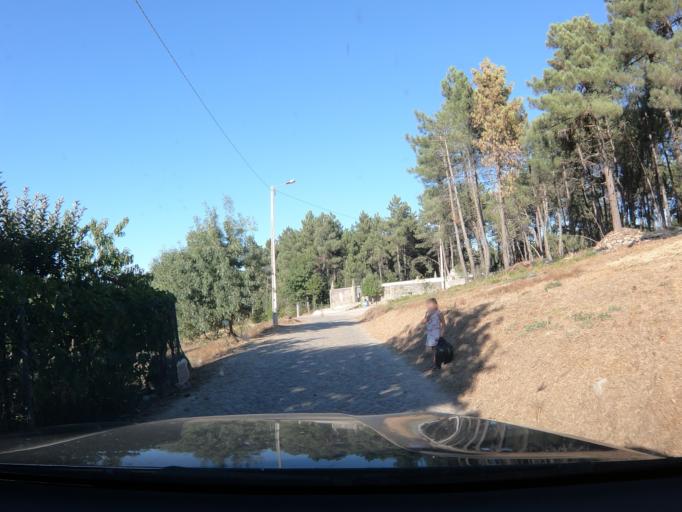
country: PT
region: Vila Real
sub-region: Sabrosa
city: Vilela
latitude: 41.2374
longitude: -7.6136
